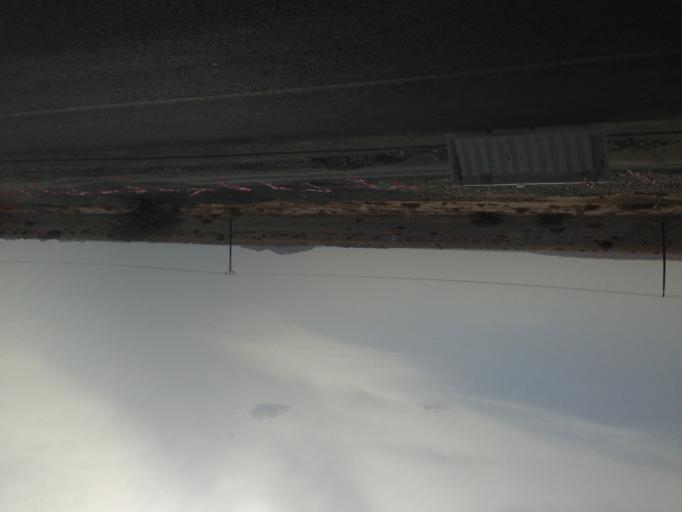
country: OM
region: Ash Sharqiyah
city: Al Qabil
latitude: 22.5490
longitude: 58.7198
